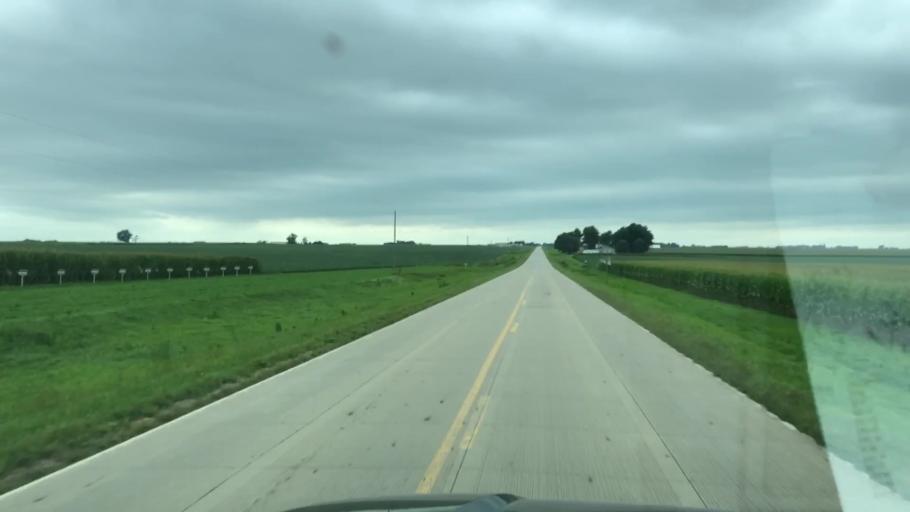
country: US
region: Iowa
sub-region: O'Brien County
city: Sheldon
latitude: 43.1404
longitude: -95.9794
